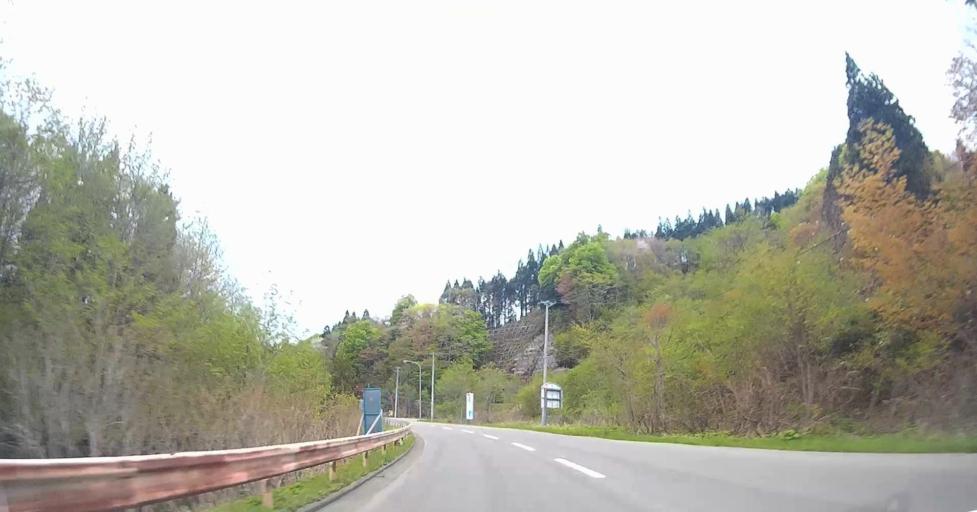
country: JP
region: Aomori
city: Goshogawara
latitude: 41.1185
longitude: 140.5237
